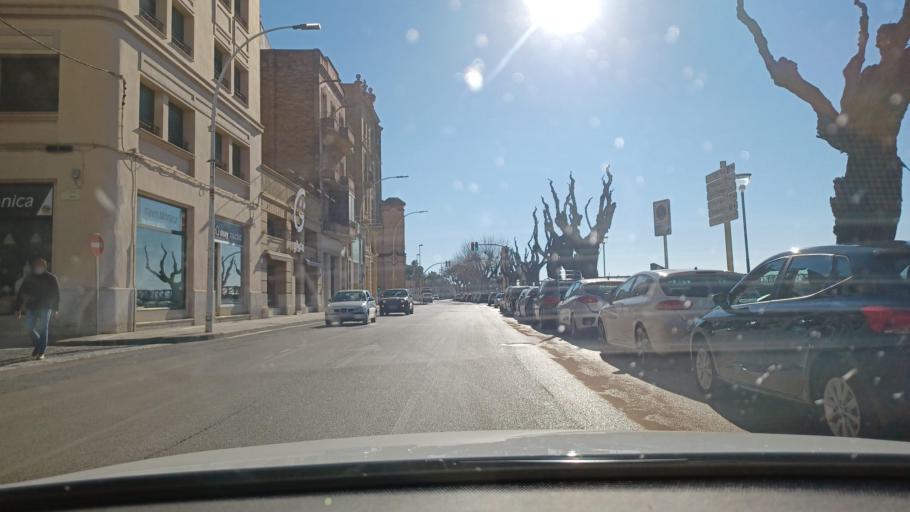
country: ES
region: Catalonia
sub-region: Provincia de Tarragona
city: Tortosa
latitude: 40.8121
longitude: 0.5197
